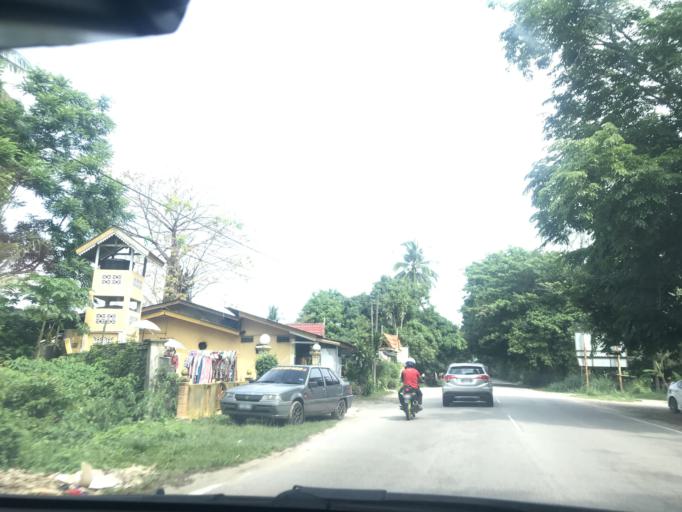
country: MY
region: Kelantan
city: Tumpat
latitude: 6.2130
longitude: 102.1299
